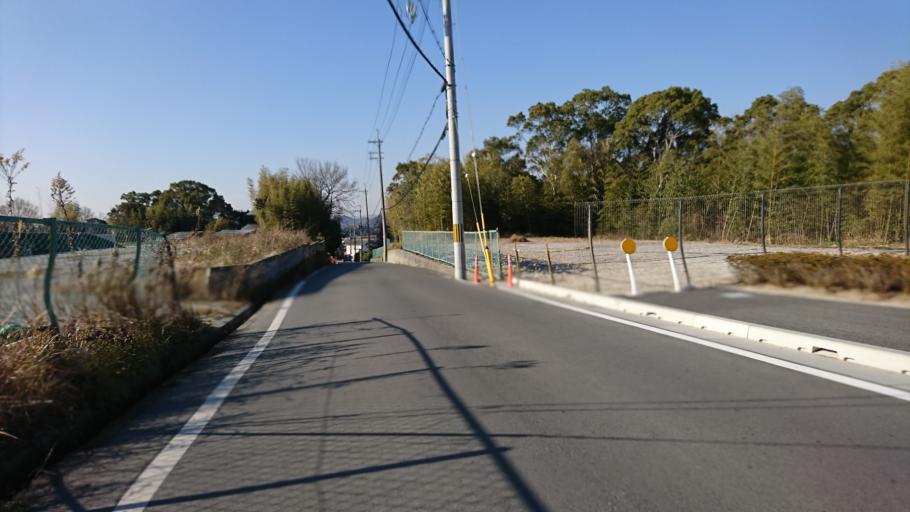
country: JP
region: Hyogo
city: Kakogawacho-honmachi
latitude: 34.7769
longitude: 134.8813
